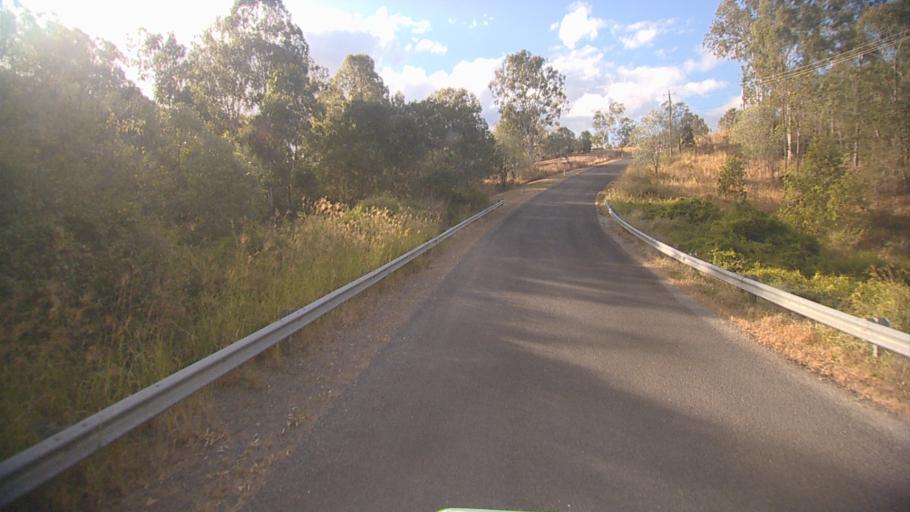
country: AU
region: Queensland
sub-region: Logan
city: Cedar Vale
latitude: -27.9053
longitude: 153.0640
